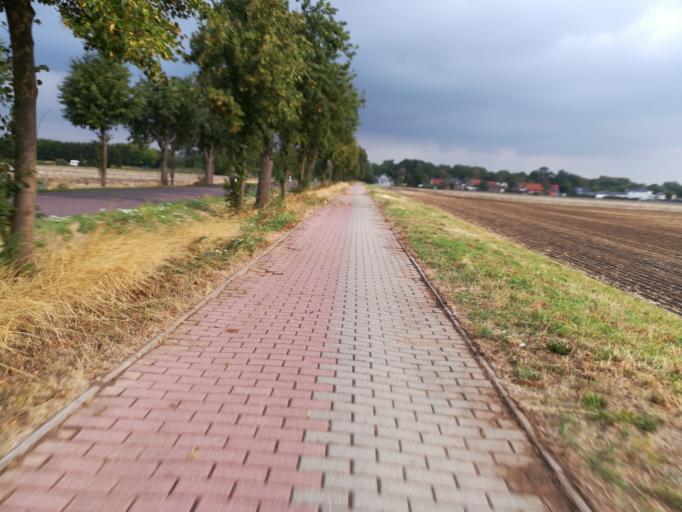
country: DE
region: Saxony-Anhalt
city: Eichenbarleben
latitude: 52.1598
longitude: 11.4039
